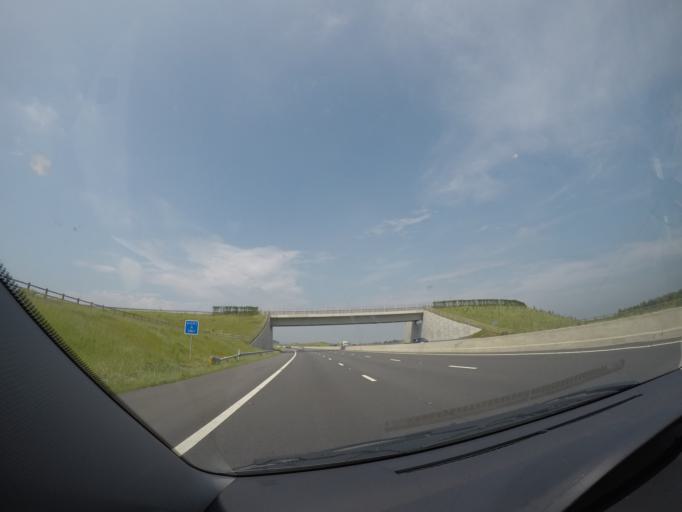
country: GB
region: England
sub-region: North Yorkshire
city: Catterick
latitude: 54.3597
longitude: -1.6202
